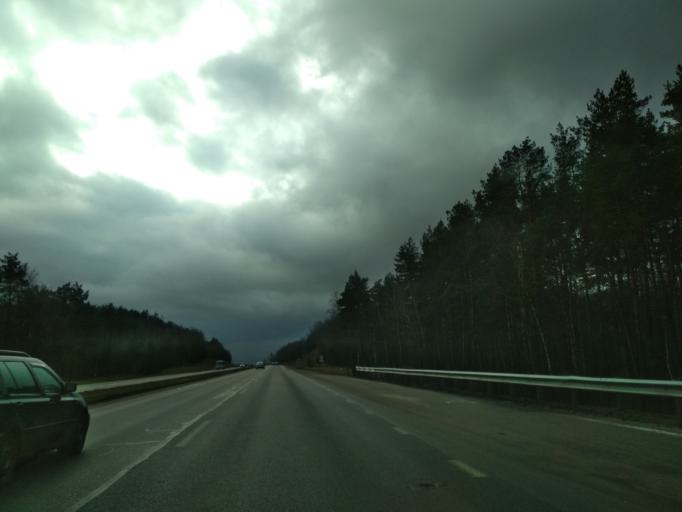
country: BY
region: Minsk
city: Luhavaya Slabada
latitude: 53.7707
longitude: 27.8271
